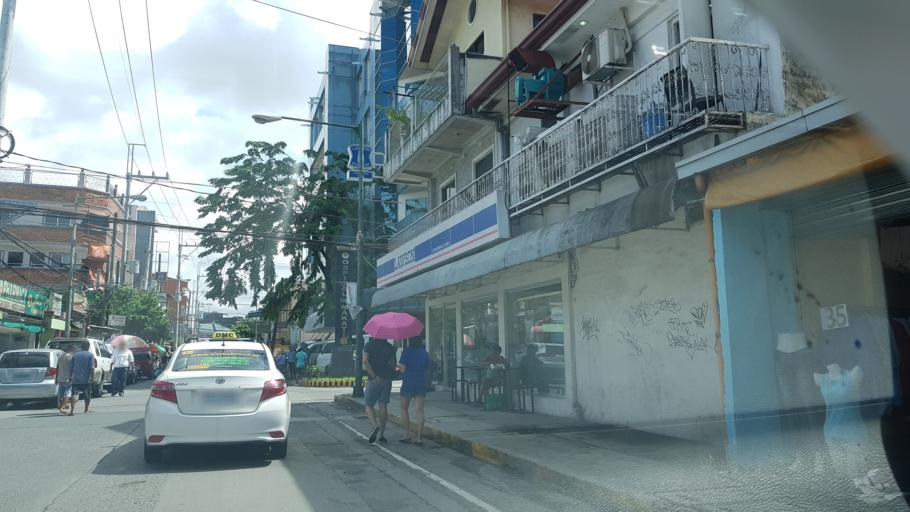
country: PH
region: Calabarzon
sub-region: Province of Rizal
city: Pateros
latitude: 14.5459
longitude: 121.0613
